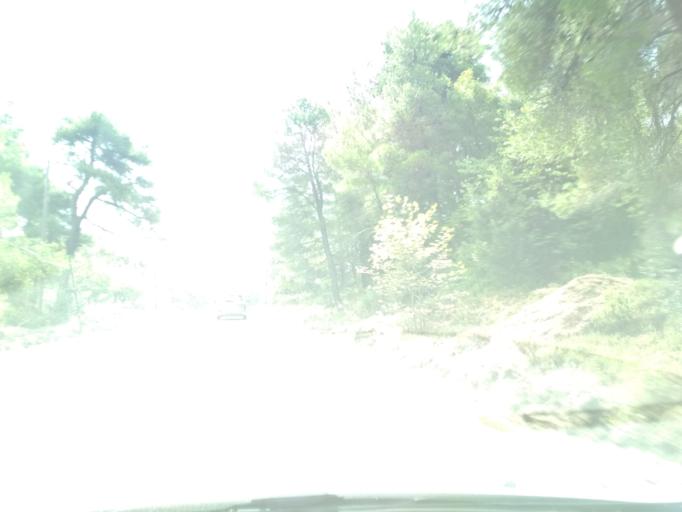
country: GR
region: Central Greece
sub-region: Nomos Evvoias
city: Politika
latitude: 38.6581
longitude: 23.5574
